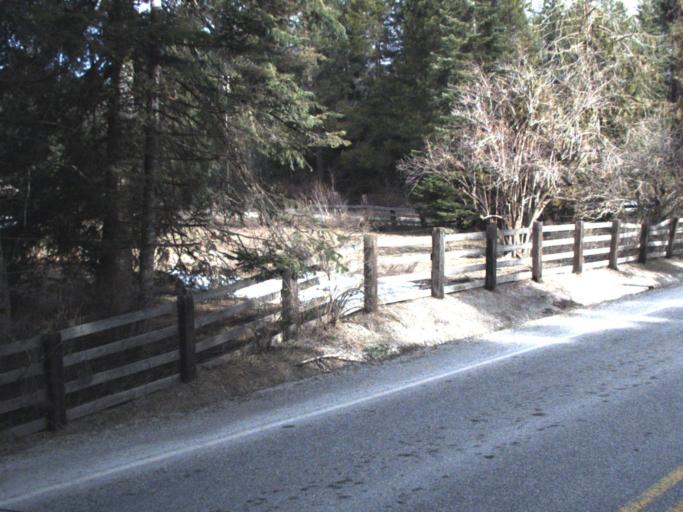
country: US
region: Washington
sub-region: Pend Oreille County
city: Newport
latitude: 48.4443
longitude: -117.3221
